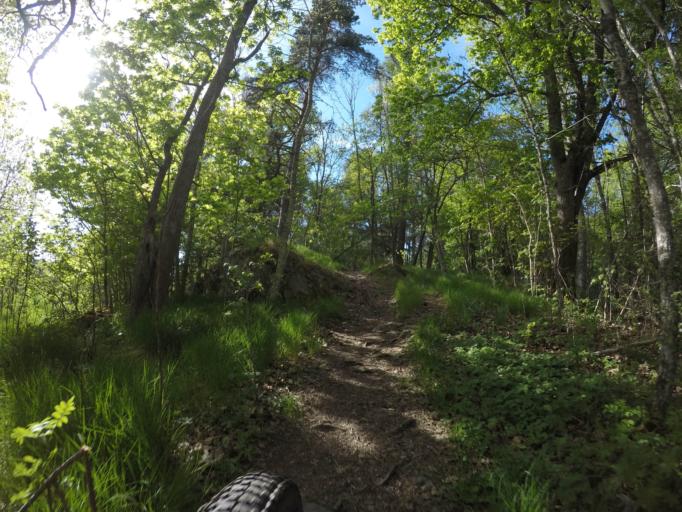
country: SE
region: Vaestmanland
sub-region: Vasteras
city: Vasteras
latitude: 59.6564
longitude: 16.5054
